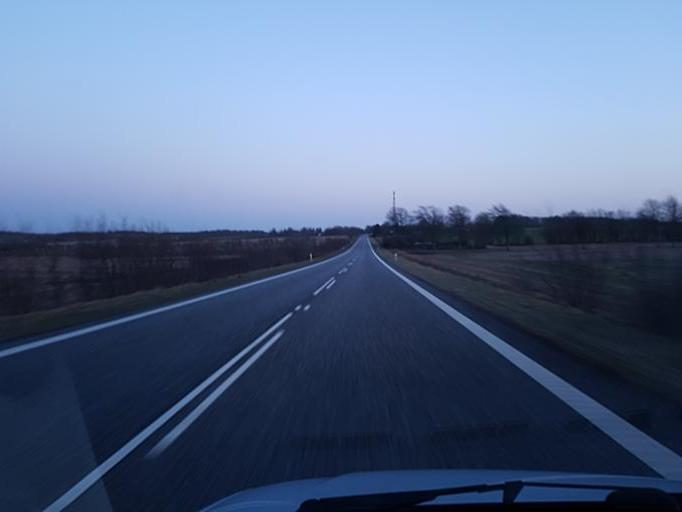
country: DK
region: Central Jutland
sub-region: Holstebro Kommune
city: Holstebro
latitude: 56.2500
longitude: 8.6082
